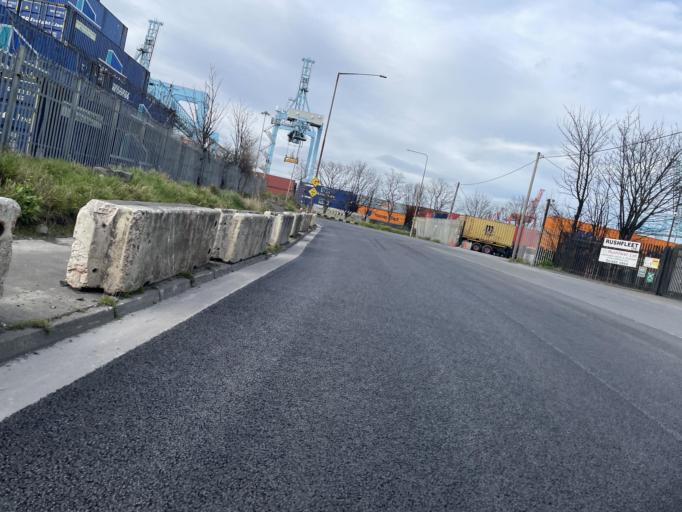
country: IE
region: Leinster
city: Sandymount
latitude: 53.3409
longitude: -6.2084
